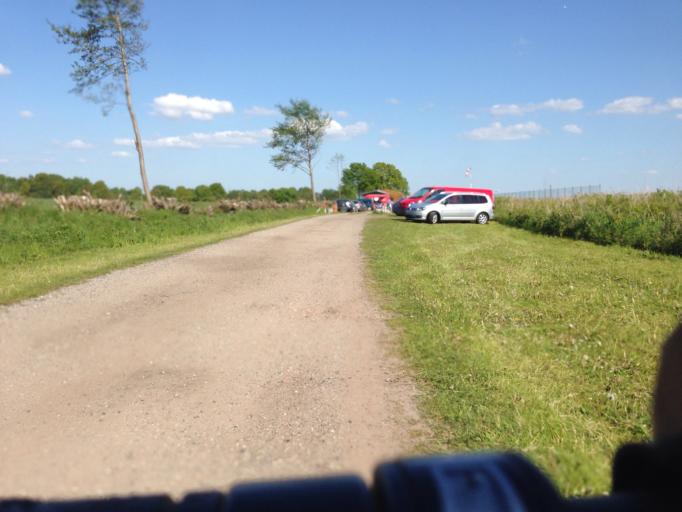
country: DE
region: Schleswig-Holstein
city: Braak
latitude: 53.6337
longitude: 10.2338
